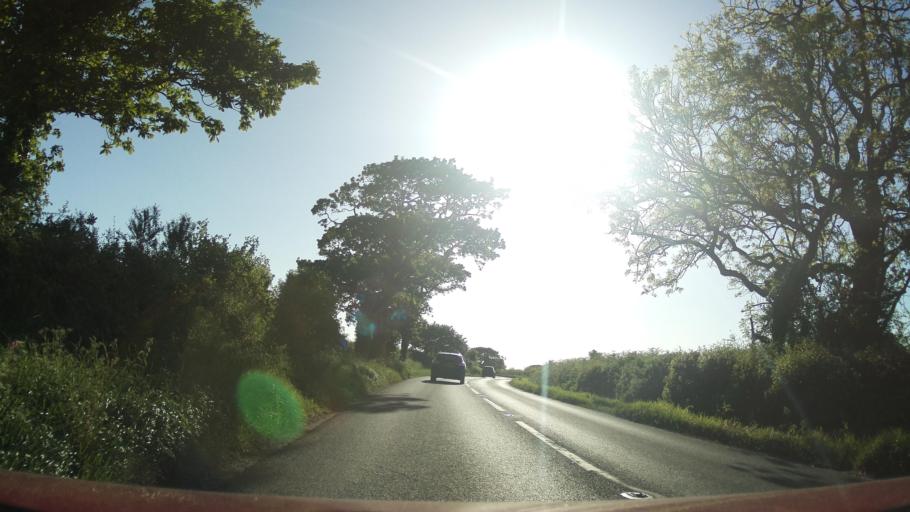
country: GB
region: England
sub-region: Devon
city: Colyton
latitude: 50.7126
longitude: -3.1335
